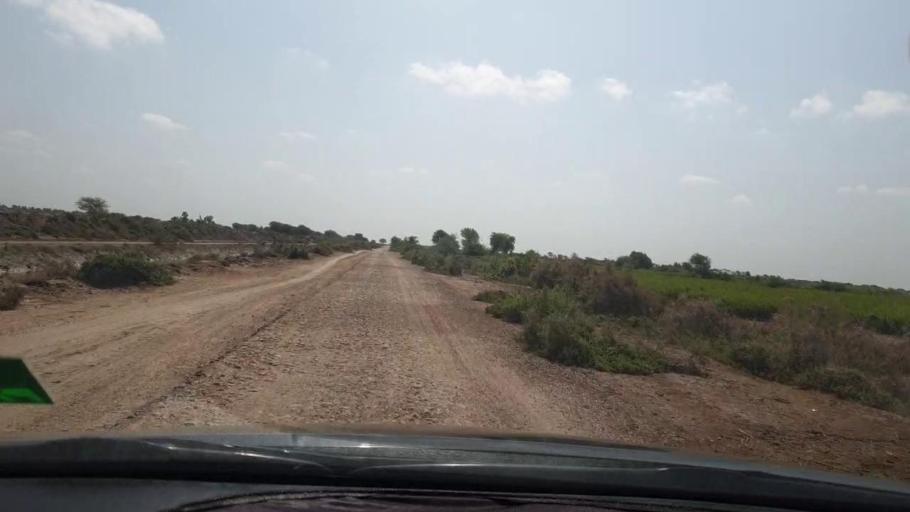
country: PK
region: Sindh
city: Tando Bago
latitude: 24.8444
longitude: 69.0394
